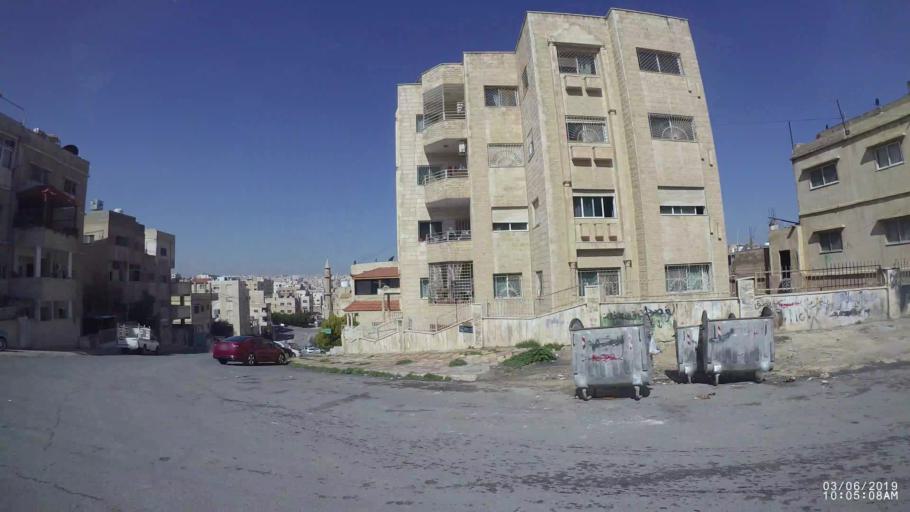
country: JO
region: Amman
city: Amman
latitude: 31.9840
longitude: 35.9849
